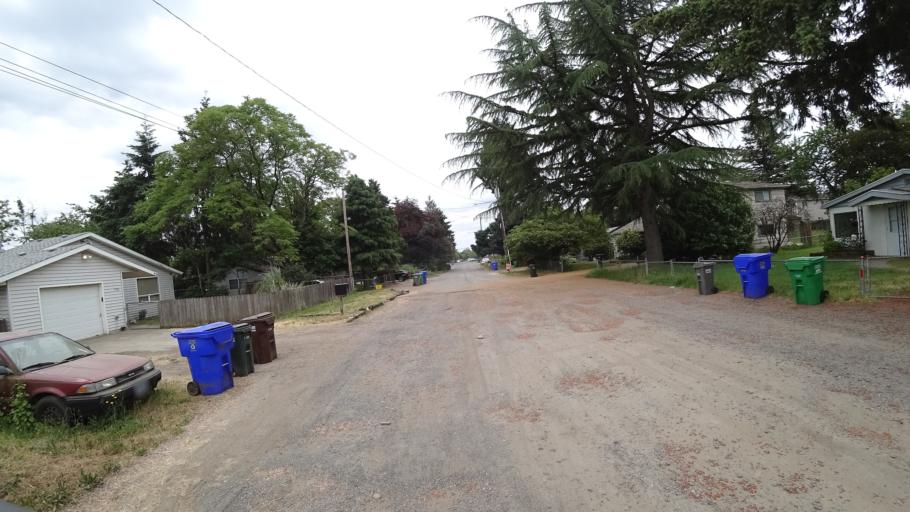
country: US
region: Oregon
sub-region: Multnomah County
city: Lents
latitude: 45.4663
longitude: -122.5861
